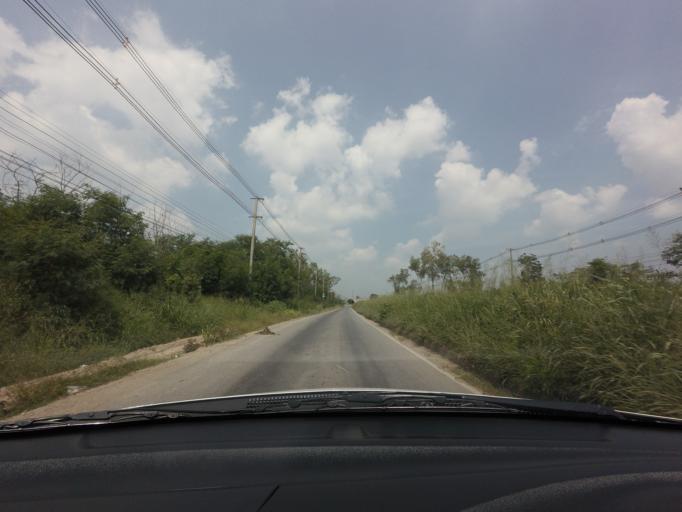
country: TH
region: Nakhon Ratchasima
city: Pak Chong
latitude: 14.6707
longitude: 101.4566
